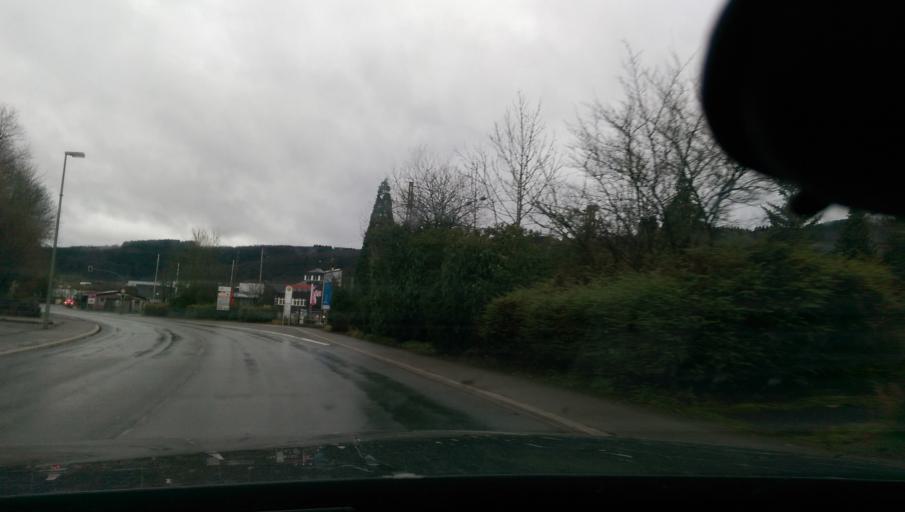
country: DE
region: North Rhine-Westphalia
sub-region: Regierungsbezirk Arnsberg
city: Finnentrop
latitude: 51.1999
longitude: 7.9645
